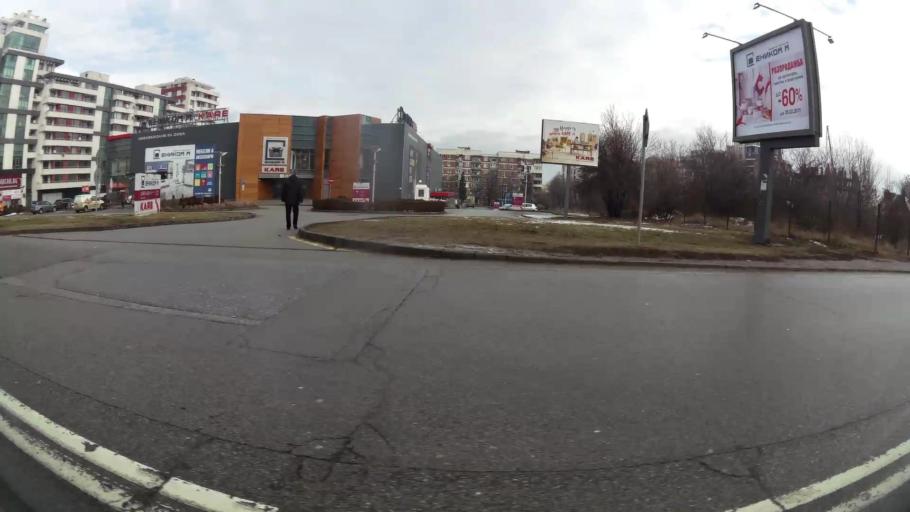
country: BG
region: Sofiya
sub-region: Obshtina Bozhurishte
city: Bozhurishte
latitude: 42.7227
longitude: 23.2495
